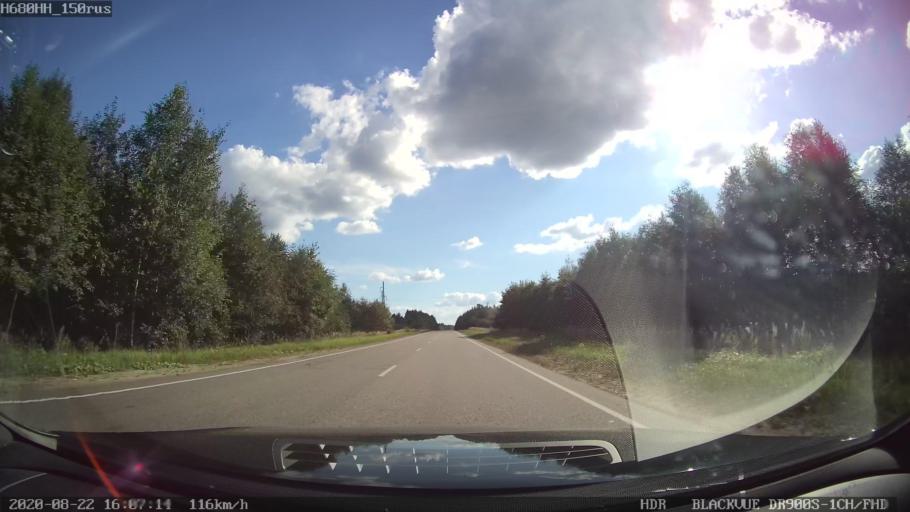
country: RU
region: Tverskaya
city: Rameshki
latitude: 57.5560
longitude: 36.3161
